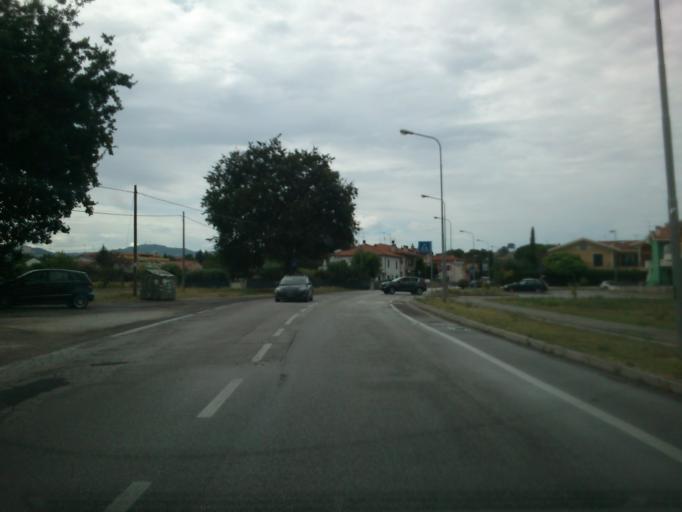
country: IT
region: The Marches
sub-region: Provincia di Pesaro e Urbino
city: Lucrezia
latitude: 43.7757
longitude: 12.9452
